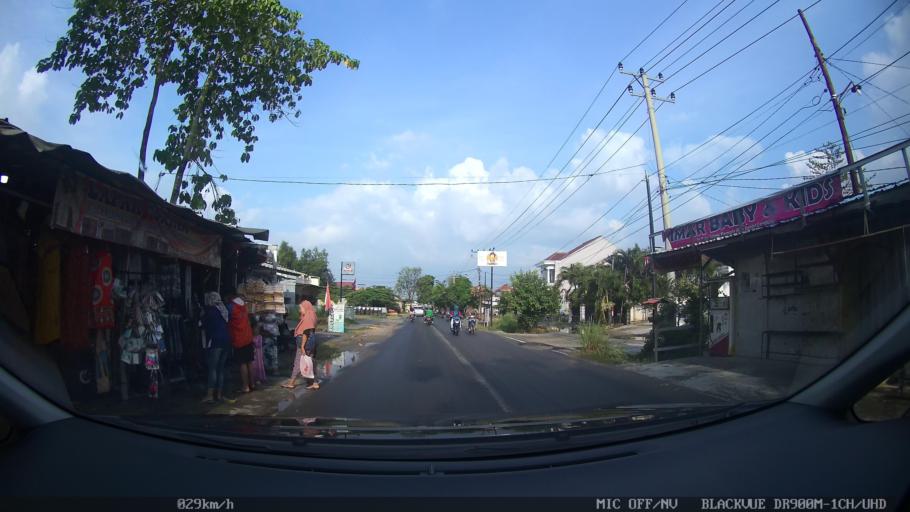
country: ID
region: Lampung
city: Kedaton
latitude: -5.3857
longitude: 105.3106
